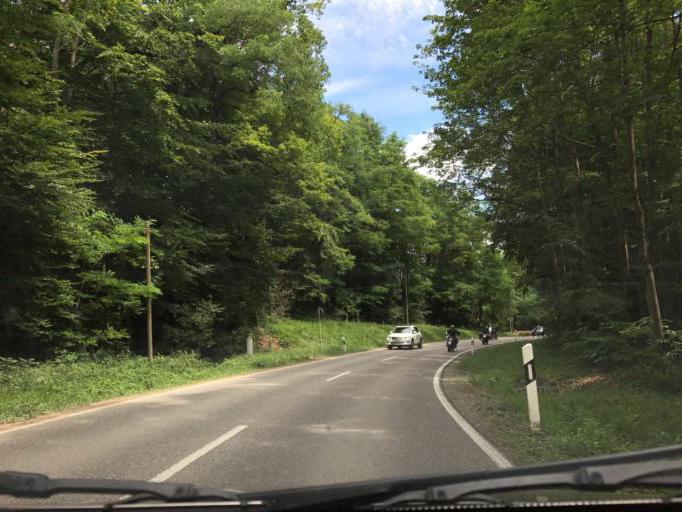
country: DE
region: Baden-Wuerttemberg
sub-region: Regierungsbezirk Stuttgart
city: Esslingen
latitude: 48.7721
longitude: 9.3229
